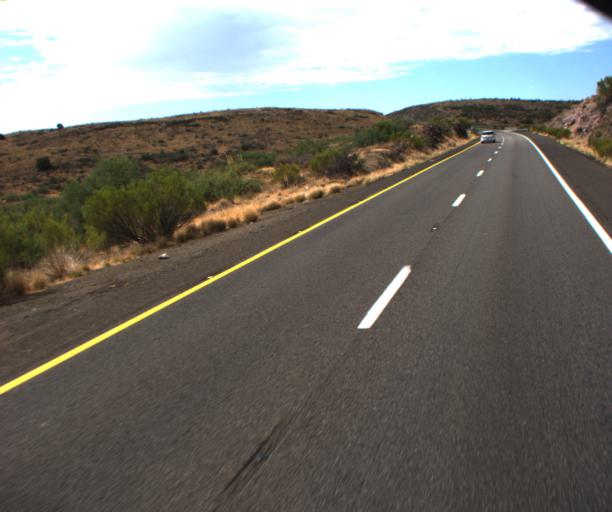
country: US
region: Arizona
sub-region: Yavapai County
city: Cordes Lakes
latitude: 34.2375
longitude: -112.1160
